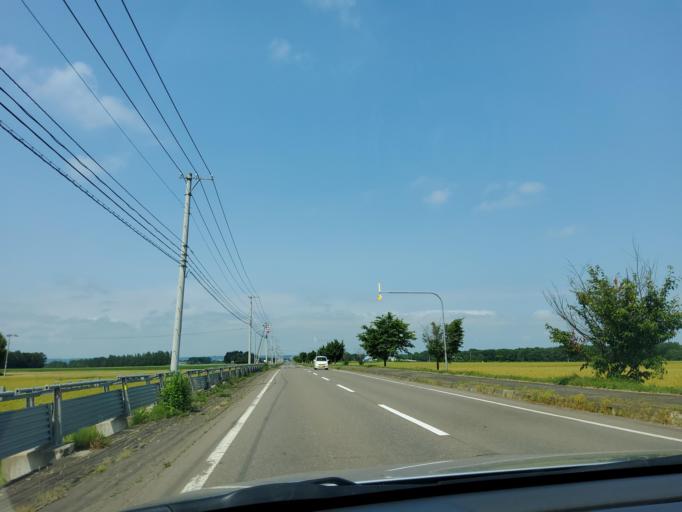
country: JP
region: Hokkaido
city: Obihiro
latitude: 42.8833
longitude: 143.0340
